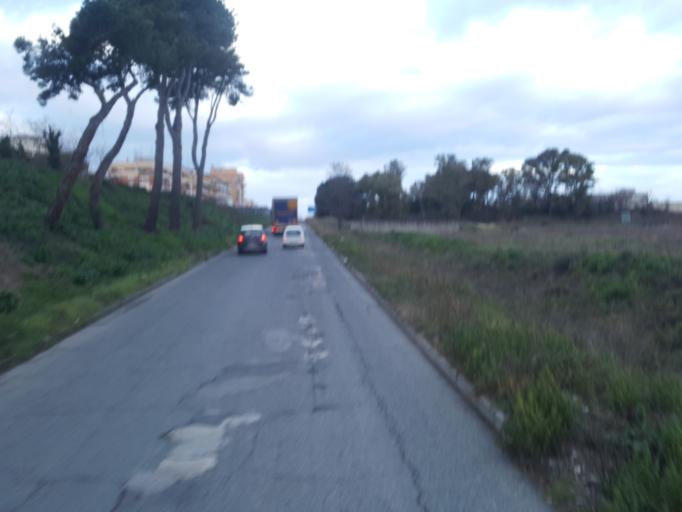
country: IT
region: Latium
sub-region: Citta metropolitana di Roma Capitale
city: Area Produttiva
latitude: 41.6737
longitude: 12.5038
